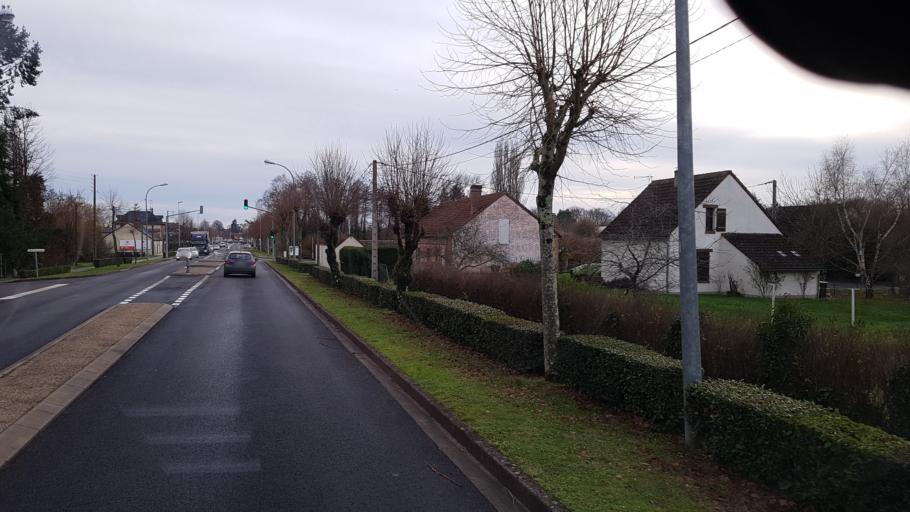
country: FR
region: Centre
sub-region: Departement du Loir-et-Cher
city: Lamotte-Beuvron
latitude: 47.6096
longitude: 2.0219
